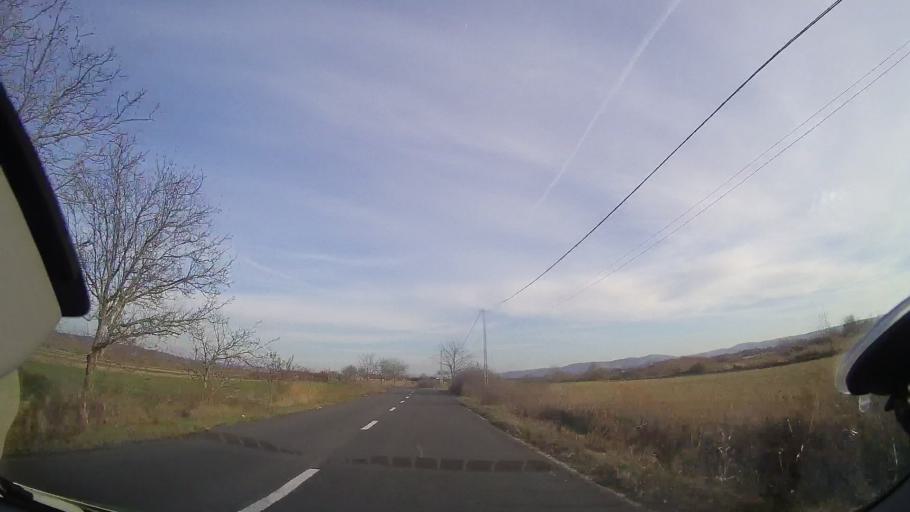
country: RO
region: Bihor
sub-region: Comuna Tileagd
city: Tileagd
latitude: 47.0639
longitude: 22.2255
